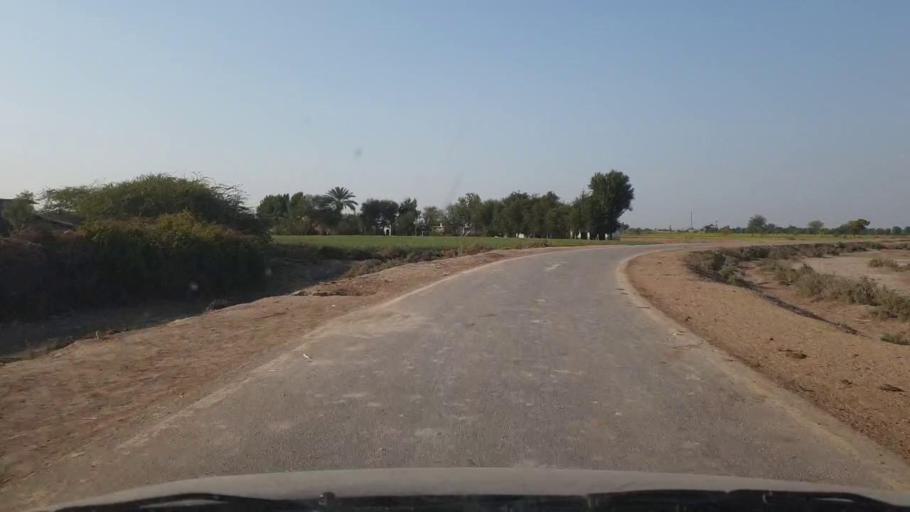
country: PK
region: Sindh
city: Samaro
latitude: 25.2895
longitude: 69.3491
